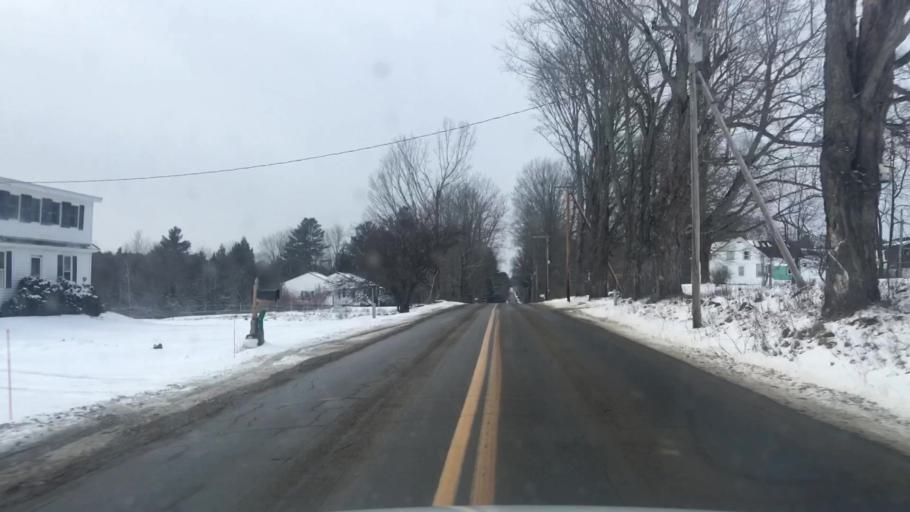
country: US
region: Maine
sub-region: Waldo County
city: Searsmont
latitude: 44.3708
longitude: -69.2039
